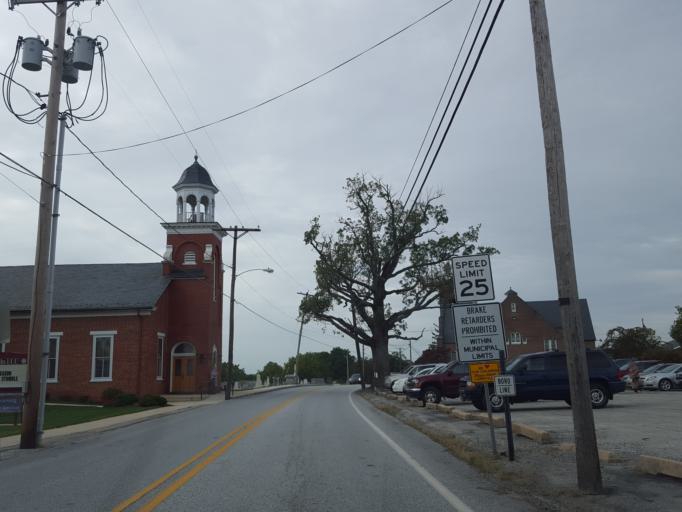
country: US
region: Pennsylvania
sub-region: York County
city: West York
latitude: 39.9034
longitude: -76.7850
